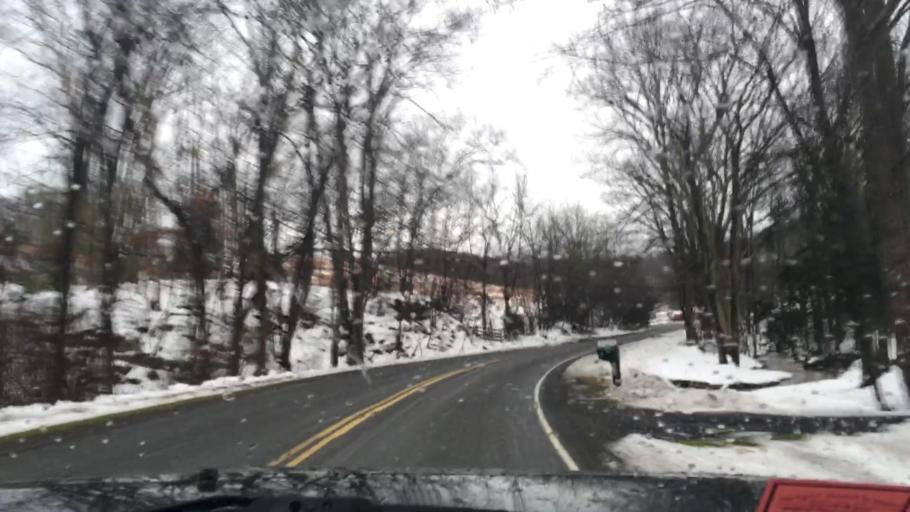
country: US
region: Virginia
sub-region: Pulaski County
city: Pulaski
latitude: 37.0119
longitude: -80.6939
